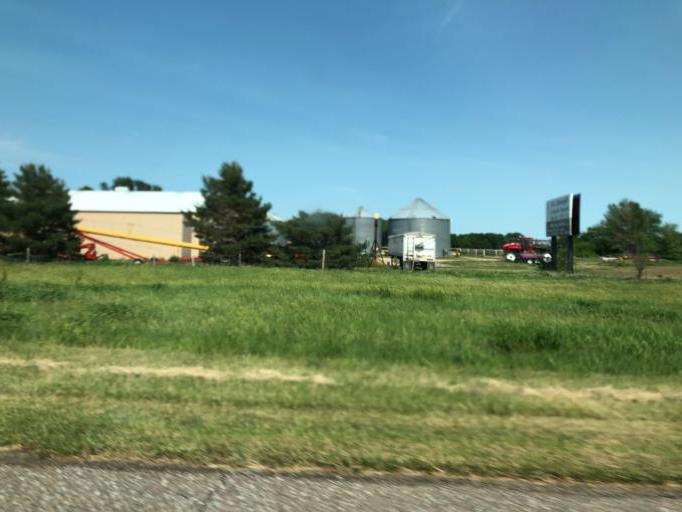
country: US
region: Nebraska
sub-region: Fillmore County
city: Geneva
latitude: 40.5229
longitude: -97.5842
